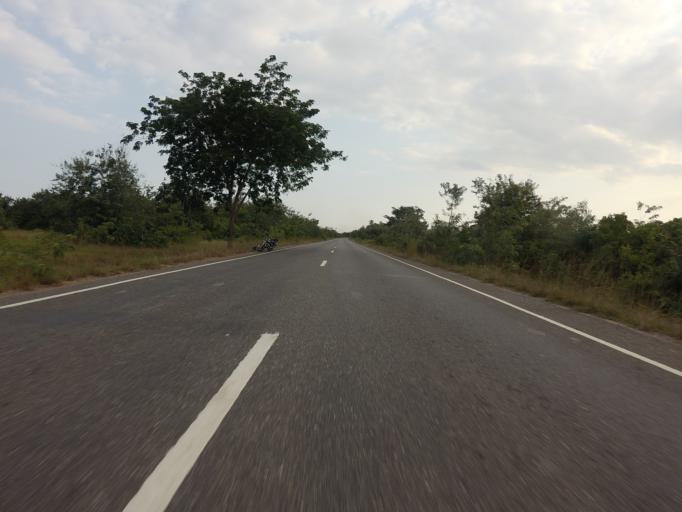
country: GH
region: Volta
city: Ho
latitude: 6.1244
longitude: 0.5217
